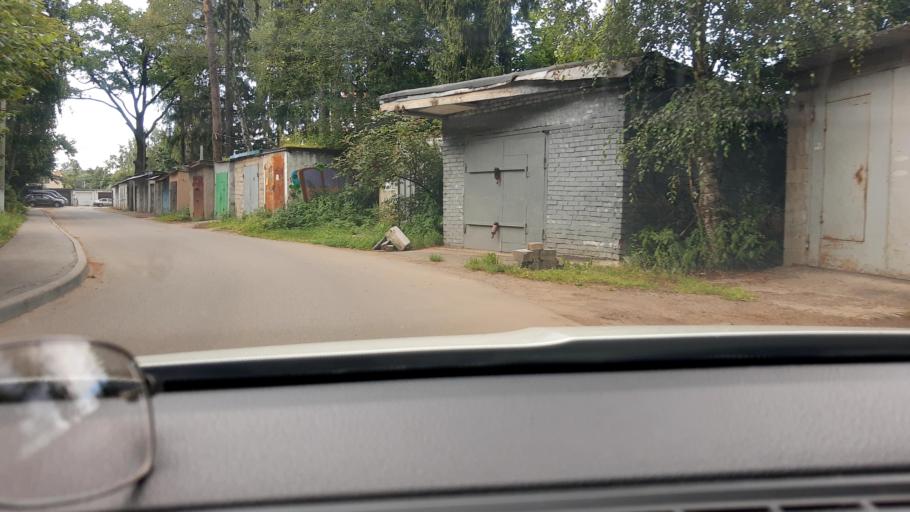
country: RU
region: Moskovskaya
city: Povedniki
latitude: 55.9732
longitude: 37.6092
